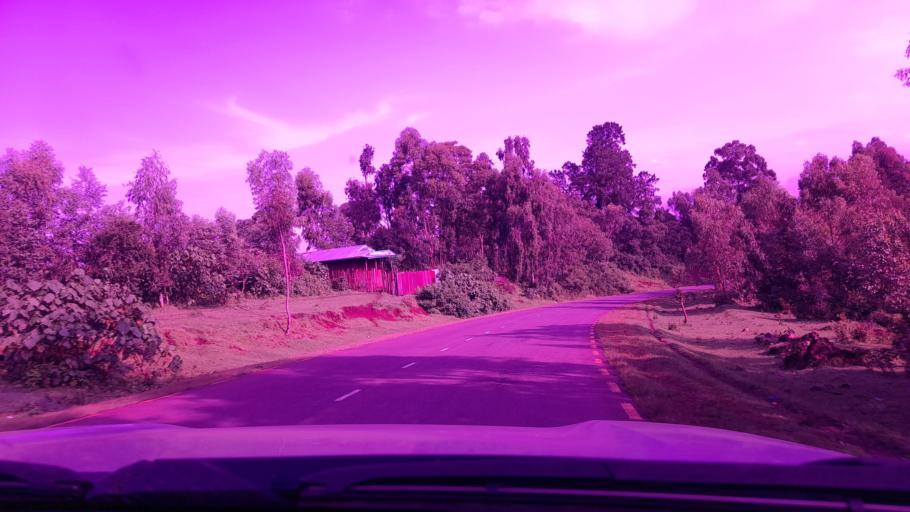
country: ET
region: Oromiya
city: Bedele
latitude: 8.1905
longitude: 36.4441
